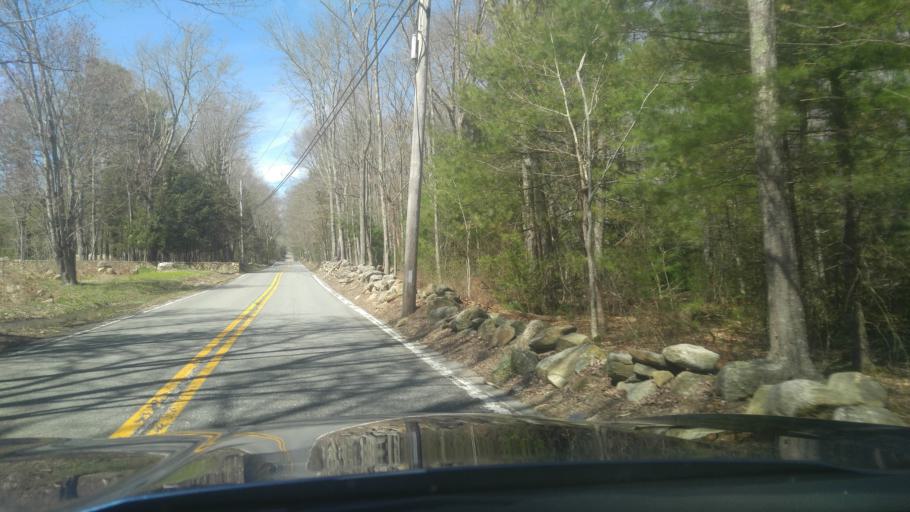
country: US
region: Rhode Island
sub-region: Washington County
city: Hope Valley
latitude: 41.5786
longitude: -71.7558
